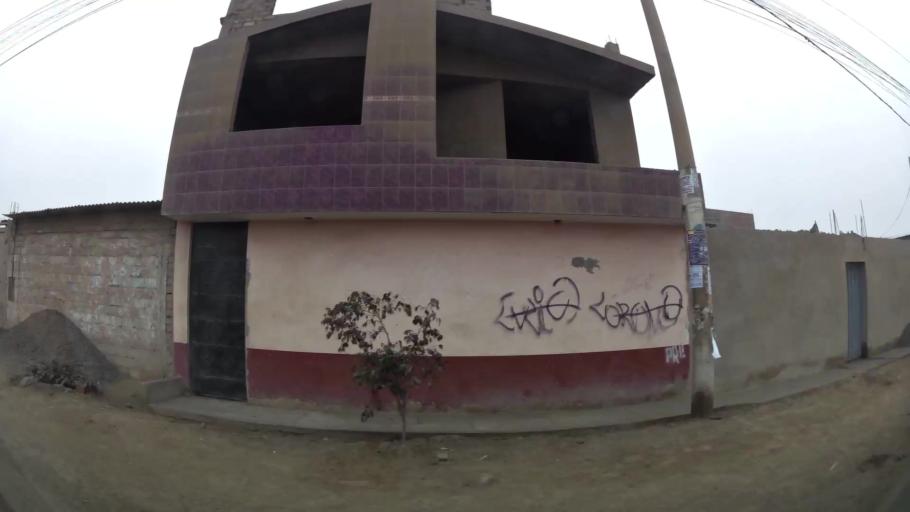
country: PE
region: Lima
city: Ventanilla
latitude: -11.8422
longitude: -77.1001
